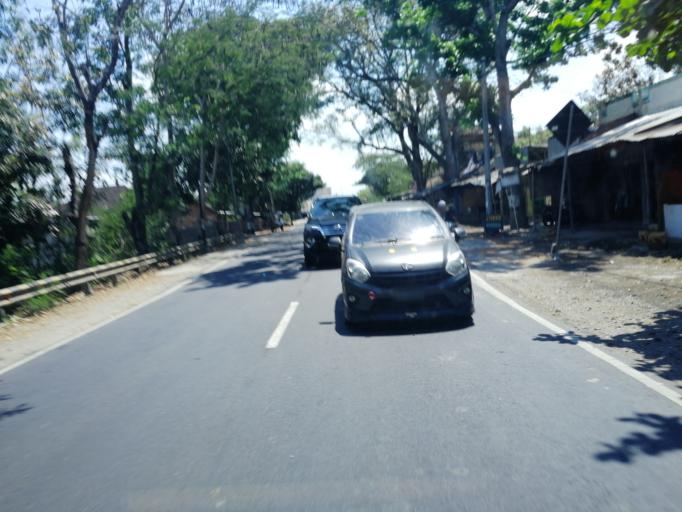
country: ID
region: West Nusa Tenggara
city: Jelateng Timur
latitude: -8.6927
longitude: 116.1099
